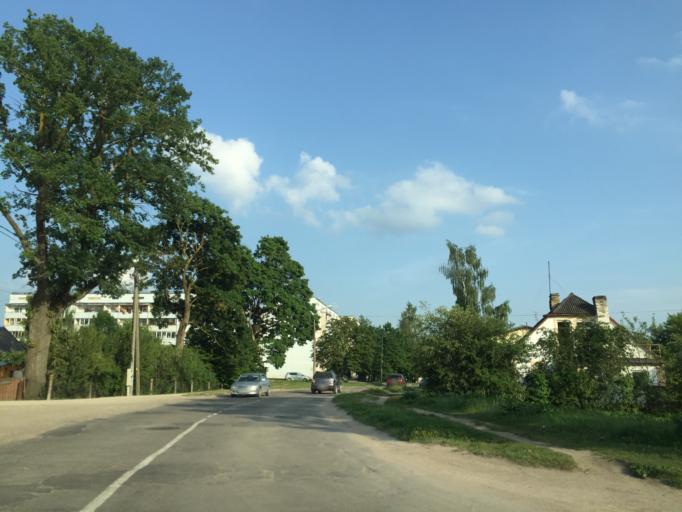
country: LV
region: Jelgava
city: Jelgava
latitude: 56.6625
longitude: 23.7029
